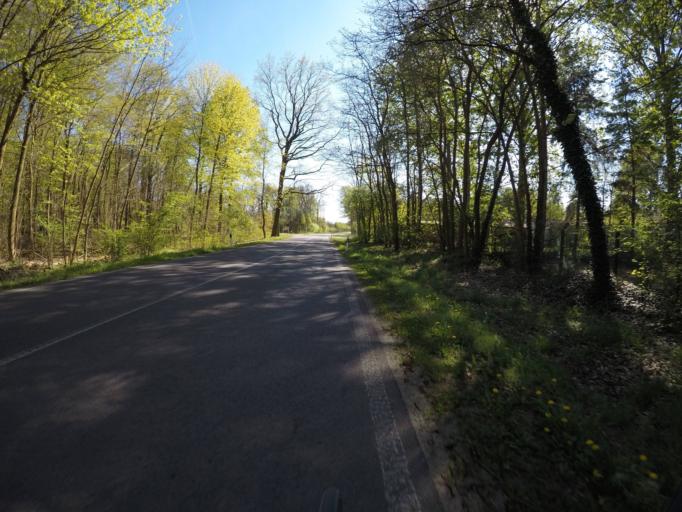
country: DE
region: Brandenburg
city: Rehfelde
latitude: 52.5401
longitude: 13.9361
